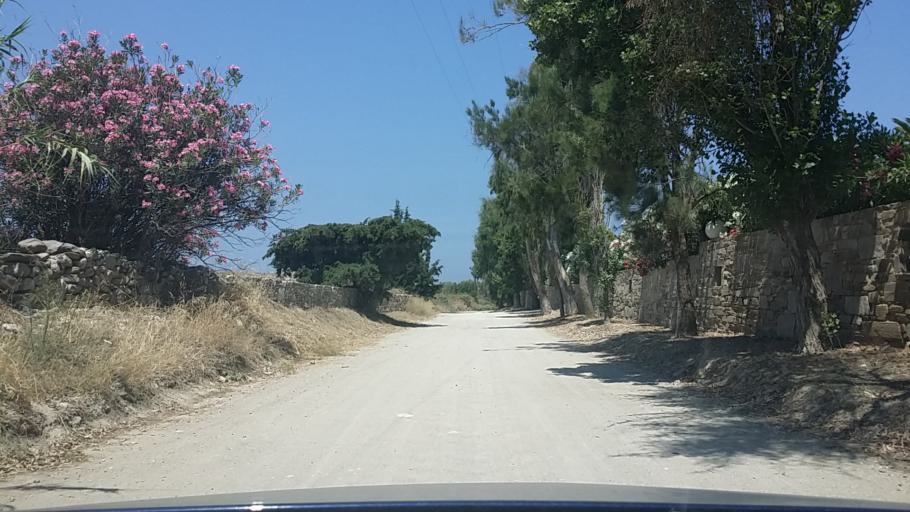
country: GR
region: South Aegean
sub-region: Nomos Kykladon
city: Paros
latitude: 37.0690
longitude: 25.1304
